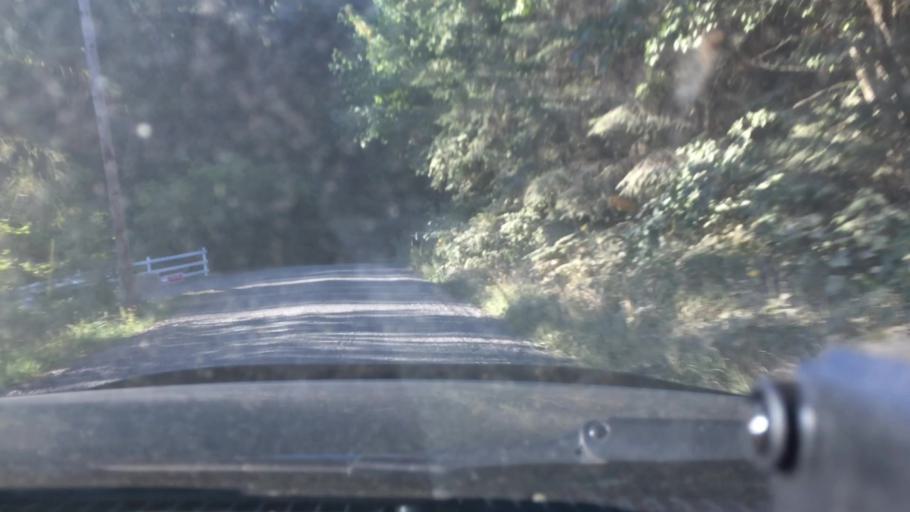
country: US
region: Oregon
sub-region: Yamhill County
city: Newberg
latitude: 45.3617
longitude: -122.9808
